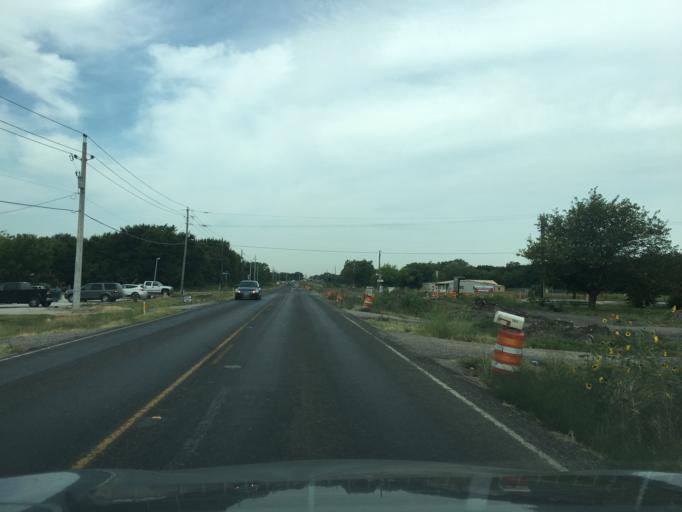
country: US
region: Texas
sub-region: Collin County
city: Lucas
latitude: 33.0550
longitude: -96.5847
